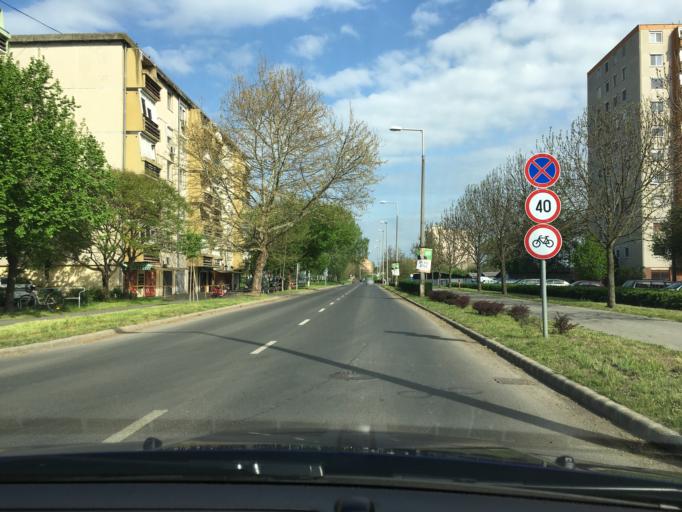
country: HU
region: Csongrad
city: Hodmezovasarhely
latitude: 46.4111
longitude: 20.3287
